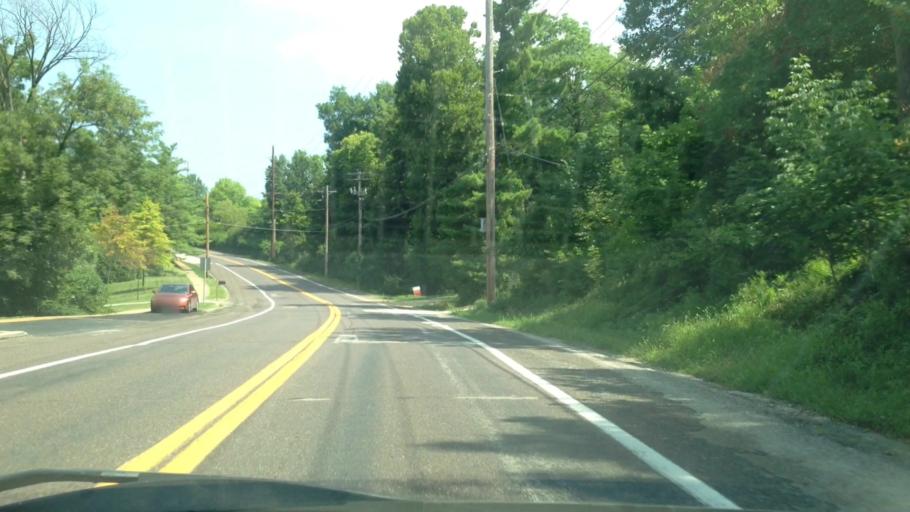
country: US
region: Missouri
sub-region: Saint Louis County
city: Des Peres
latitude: 38.5890
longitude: -90.4447
